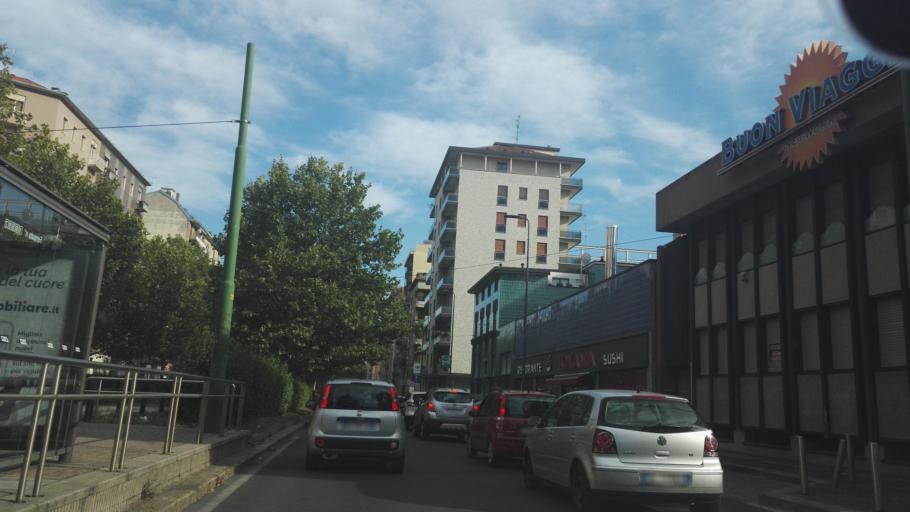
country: IT
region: Lombardy
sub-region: Citta metropolitana di Milano
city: Milano
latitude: 45.4575
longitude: 9.1512
